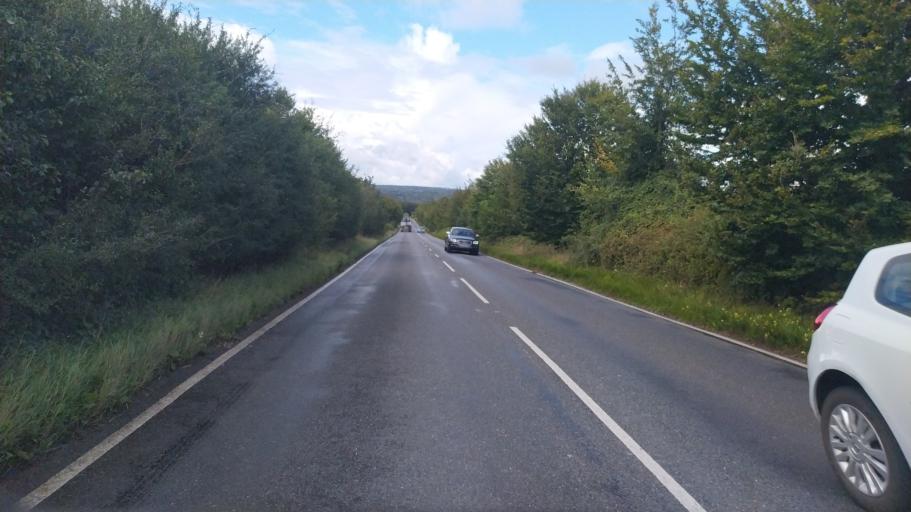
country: GB
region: England
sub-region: Dorset
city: Blandford Forum
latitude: 50.8585
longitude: -2.1403
